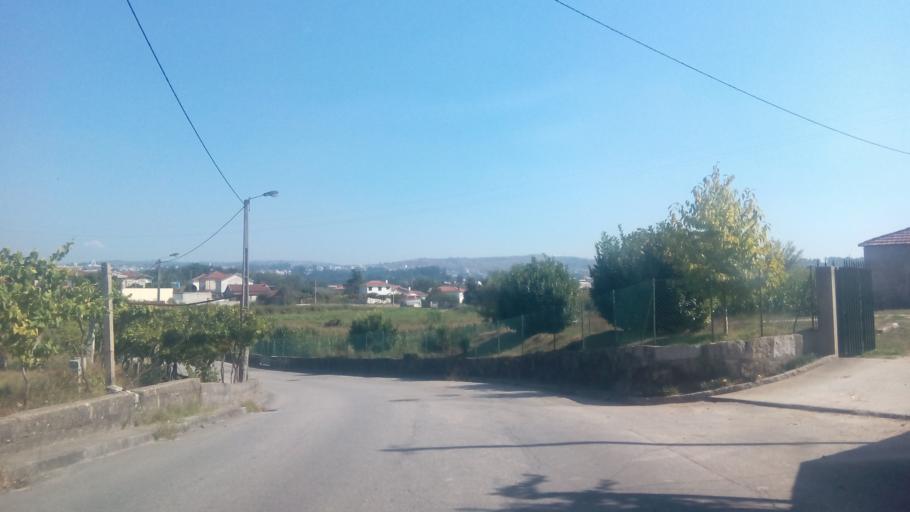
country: PT
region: Porto
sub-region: Paredes
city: Madalena
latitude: 41.2146
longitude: -8.3318
